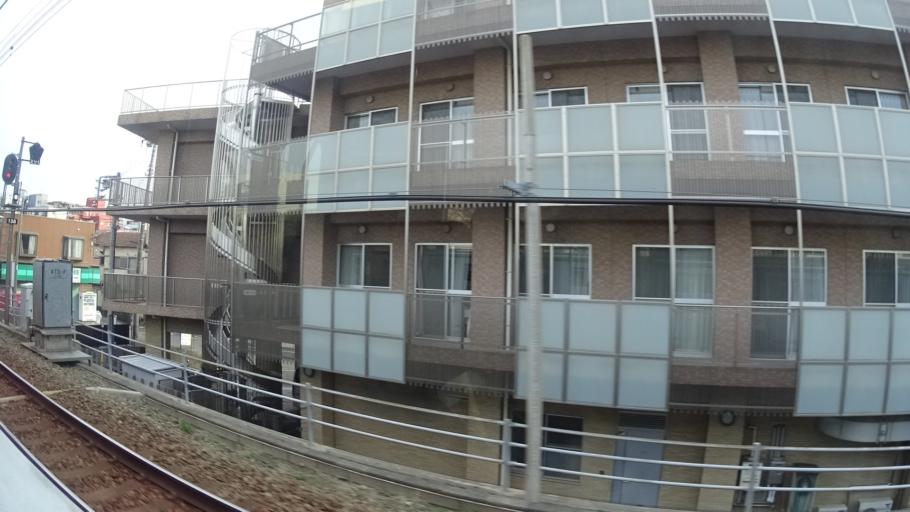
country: JP
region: Kanagawa
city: Minami-rinkan
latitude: 35.4690
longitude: 139.4995
